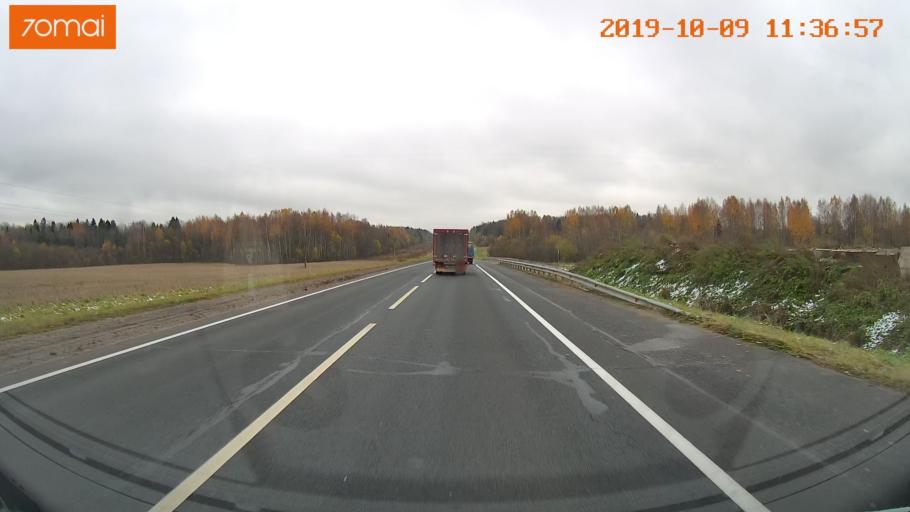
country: RU
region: Vologda
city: Gryazovets
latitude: 58.9846
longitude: 40.1419
